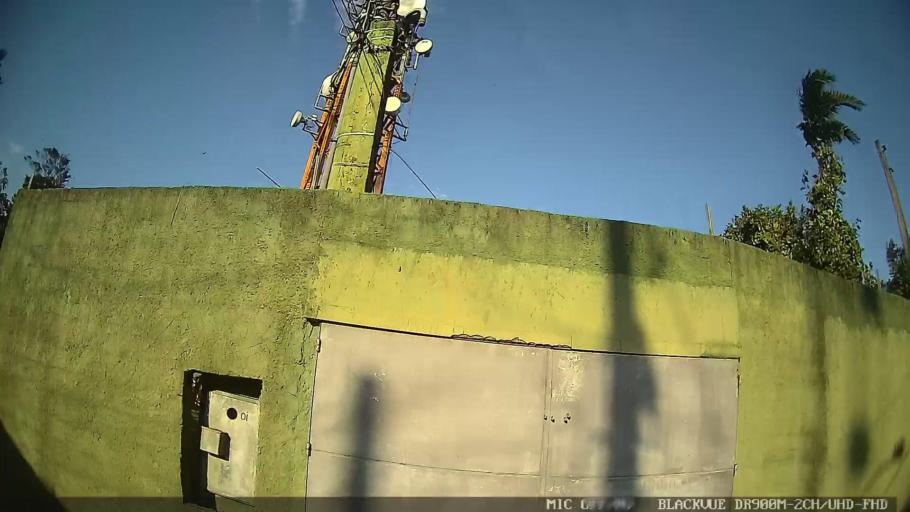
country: BR
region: Sao Paulo
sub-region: Guaruja
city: Guaruja
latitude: -23.9822
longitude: -46.2553
